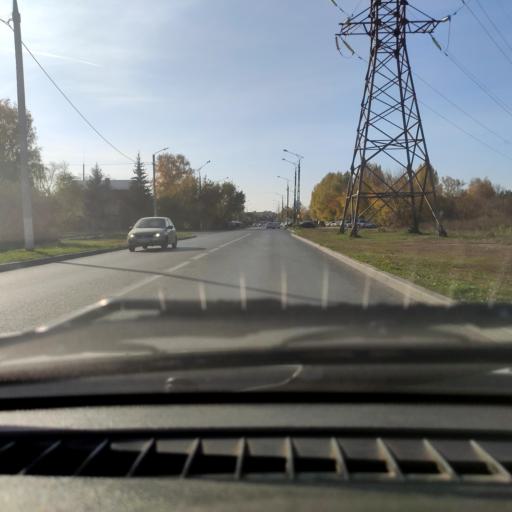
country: RU
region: Samara
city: Tol'yatti
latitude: 53.5148
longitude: 49.3954
